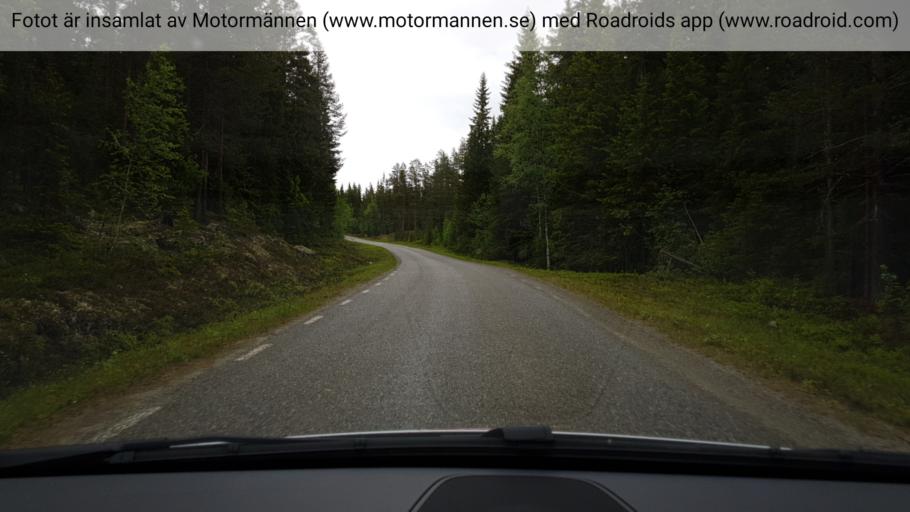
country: SE
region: Jaemtland
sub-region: Harjedalens Kommun
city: Sveg
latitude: 62.2431
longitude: 13.3636
